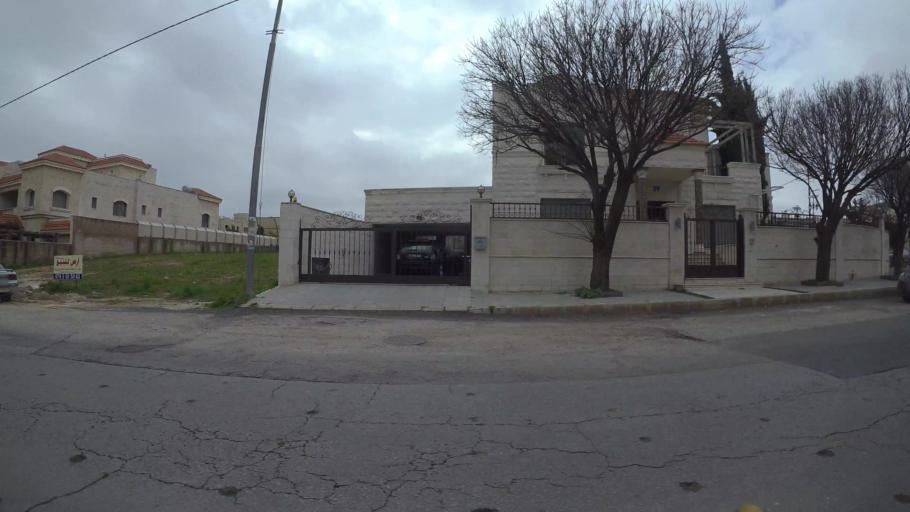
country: JO
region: Amman
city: Wadi as Sir
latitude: 31.9878
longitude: 35.8370
